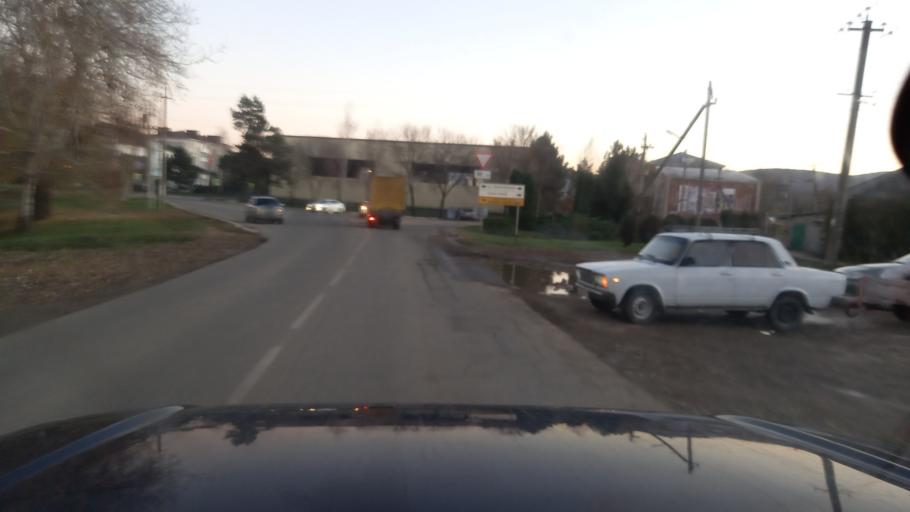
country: RU
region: Krasnodarskiy
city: Goryachiy Klyuch
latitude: 44.6327
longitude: 39.1189
